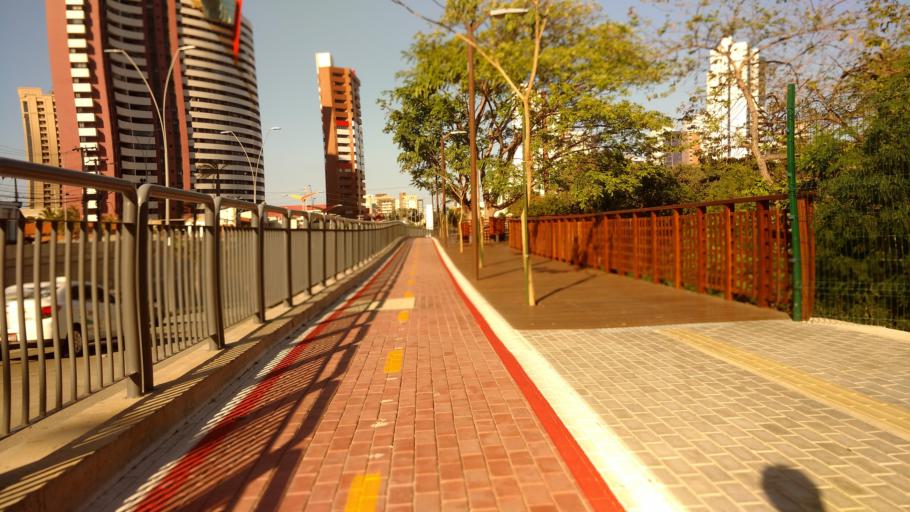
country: BR
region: Ceara
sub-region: Fortaleza
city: Fortaleza
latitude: -3.7450
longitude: -38.4886
